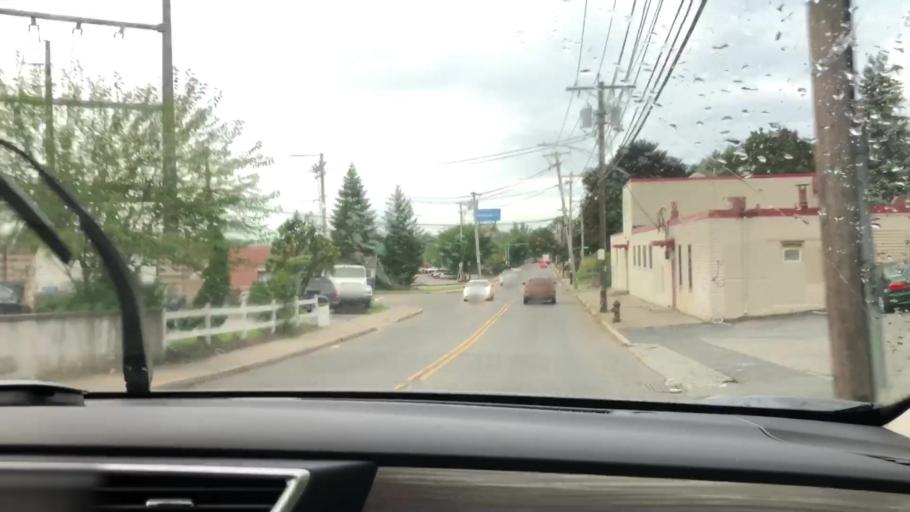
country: US
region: Rhode Island
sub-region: Providence County
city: Providence
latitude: 41.8471
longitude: -71.4158
